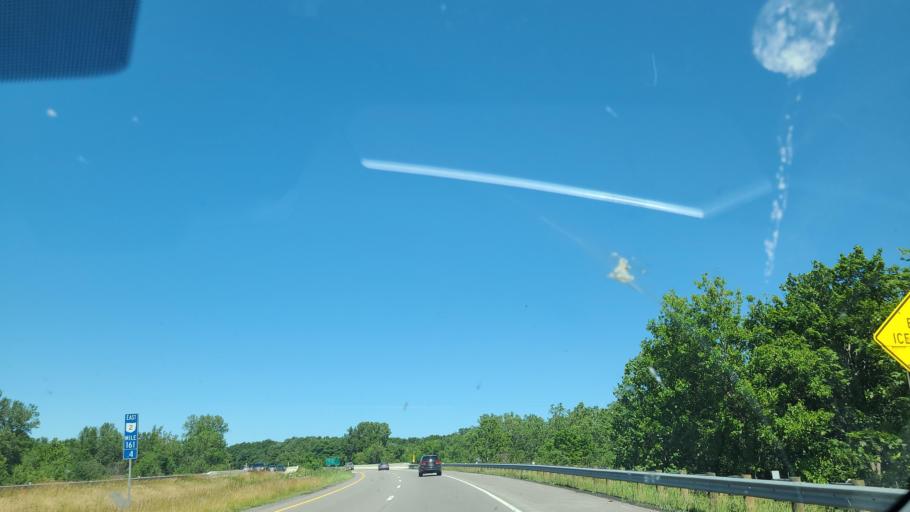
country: US
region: Ohio
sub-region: Lorain County
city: Amherst
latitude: 41.4023
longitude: -82.2613
